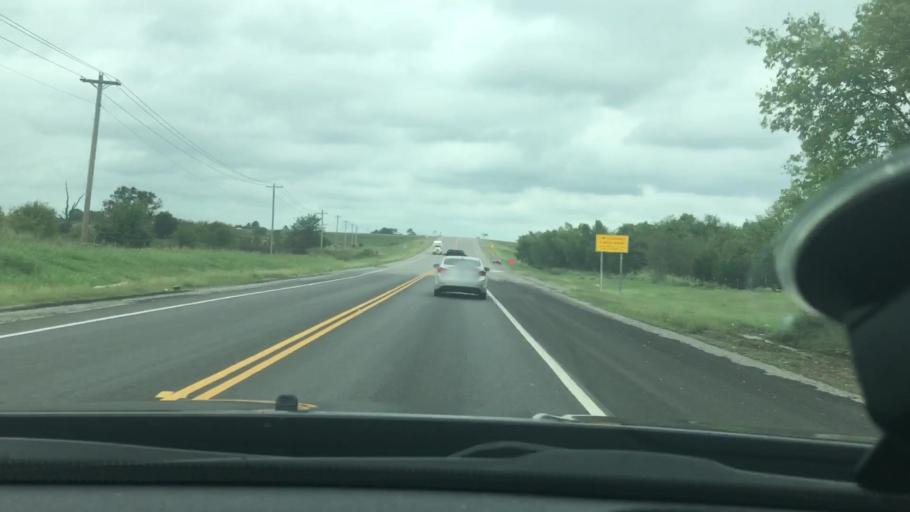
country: US
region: Oklahoma
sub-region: Bryan County
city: Durant
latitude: 33.9593
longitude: -96.3732
